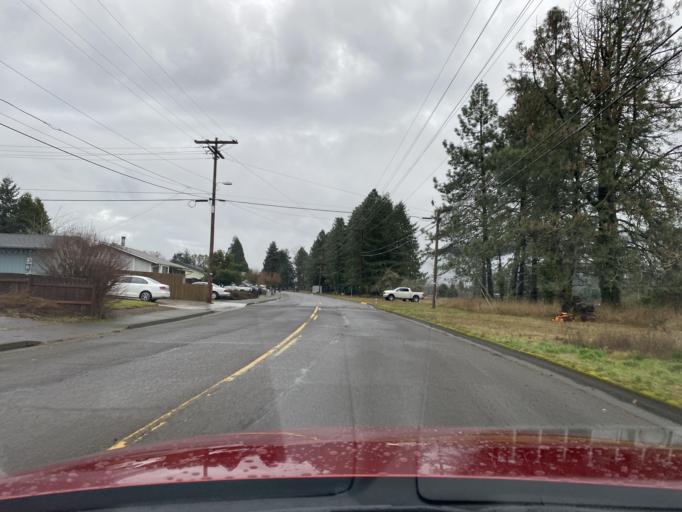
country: US
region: Oregon
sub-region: Lane County
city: Oakridge
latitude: 43.7490
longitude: -122.4817
